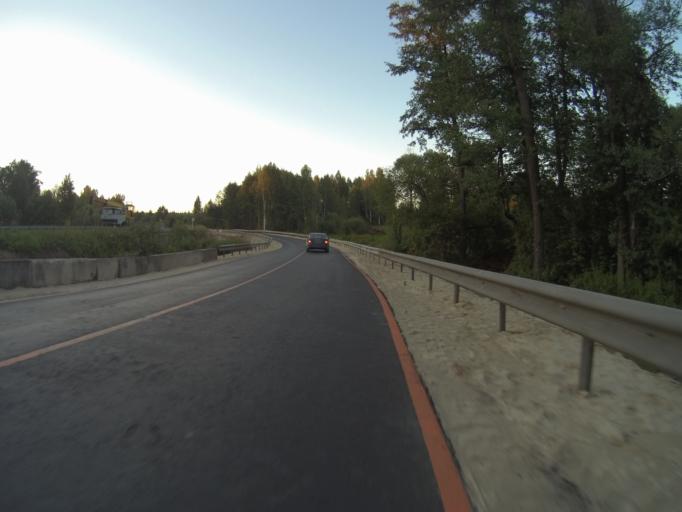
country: RU
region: Vladimir
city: Anopino
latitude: 55.8515
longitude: 40.6451
